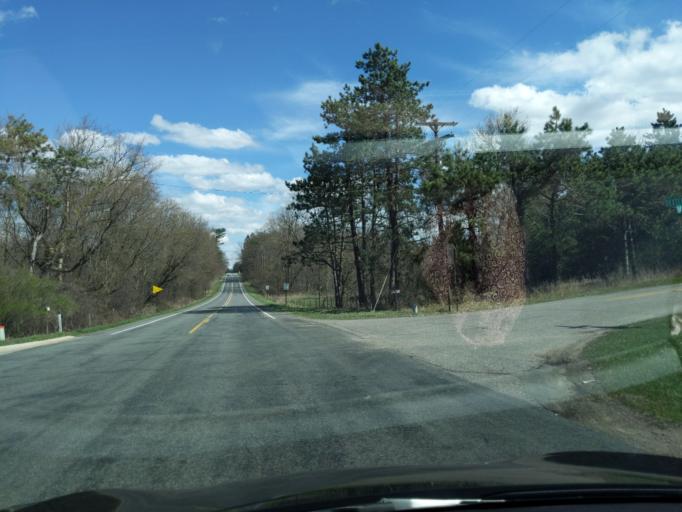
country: US
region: Michigan
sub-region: Ingham County
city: Mason
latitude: 42.5523
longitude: -84.3890
